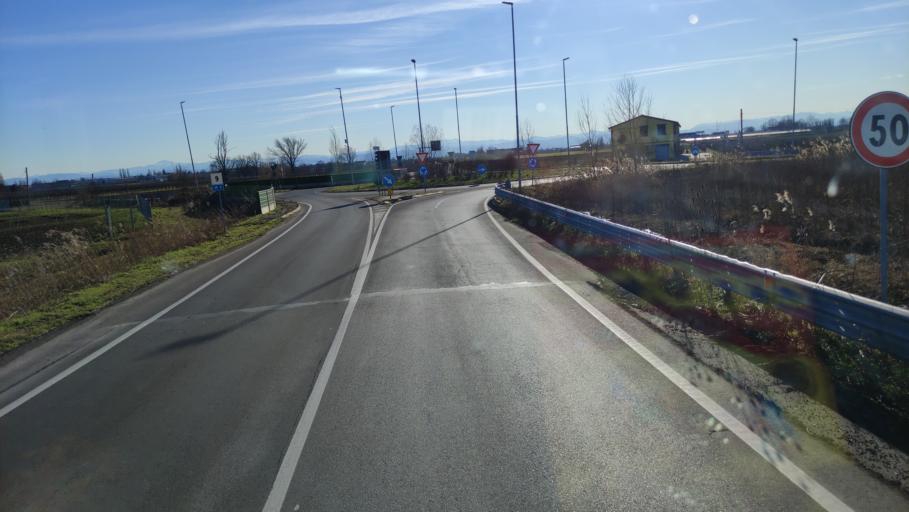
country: IT
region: Emilia-Romagna
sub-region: Provincia di Reggio Emilia
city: Bagnolo in Piano
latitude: 44.8090
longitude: 10.6868
